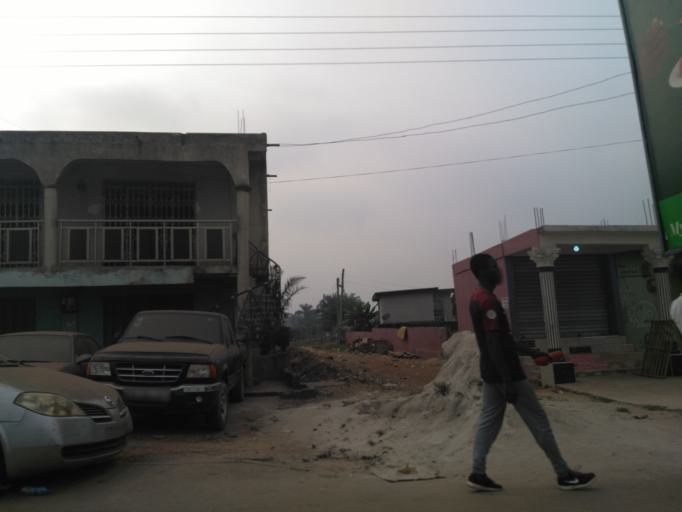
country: GH
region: Ashanti
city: Tafo
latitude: 6.7087
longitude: -1.6006
